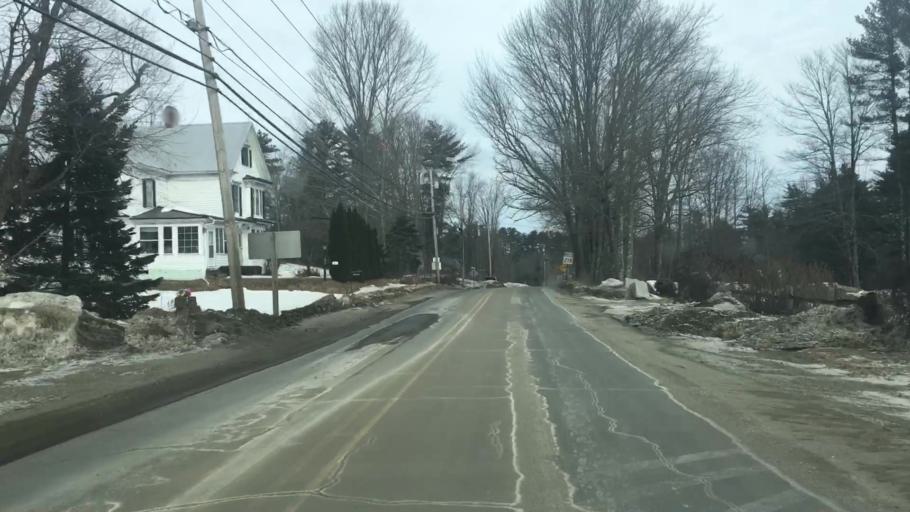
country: US
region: Maine
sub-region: Lincoln County
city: Whitefield
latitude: 44.2227
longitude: -69.5875
